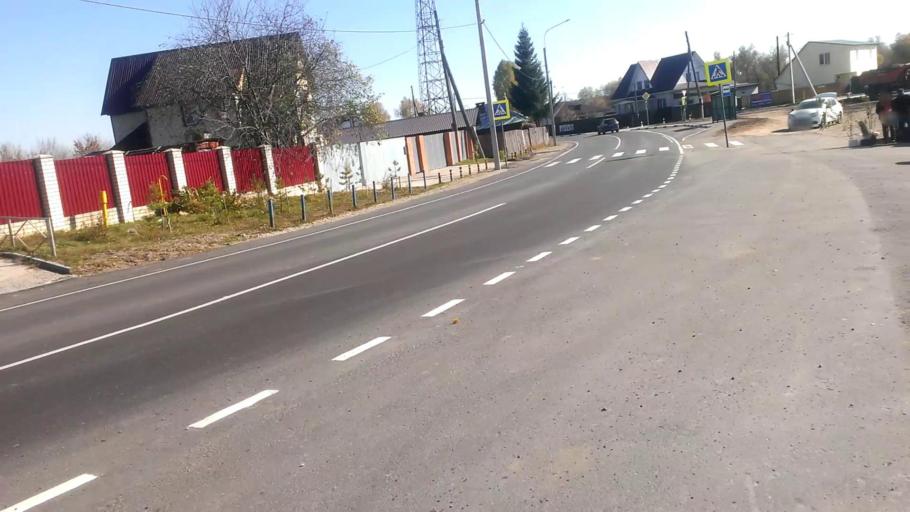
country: RU
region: Altai Krai
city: Sannikovo
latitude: 53.3185
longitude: 83.9442
